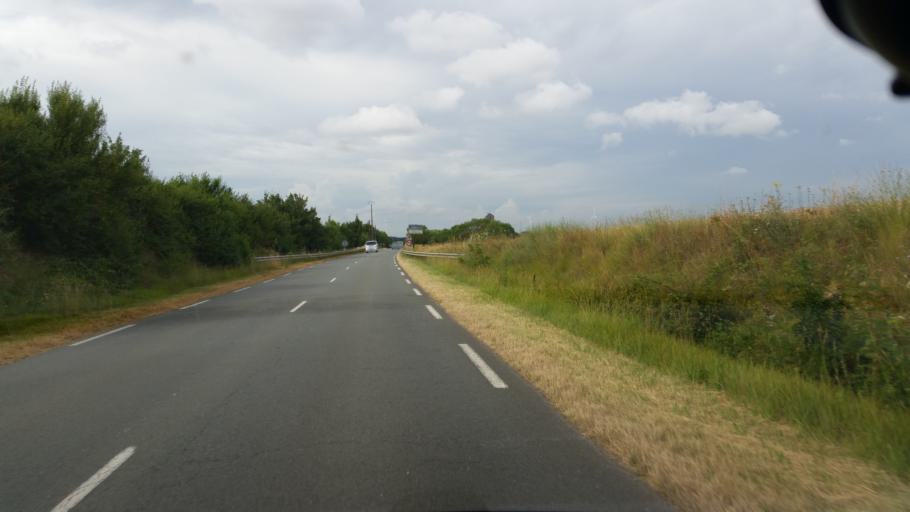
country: FR
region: Poitou-Charentes
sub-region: Departement de la Charente-Maritime
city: Saint-Jean-de-Liversay
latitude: 46.2093
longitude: -0.8752
